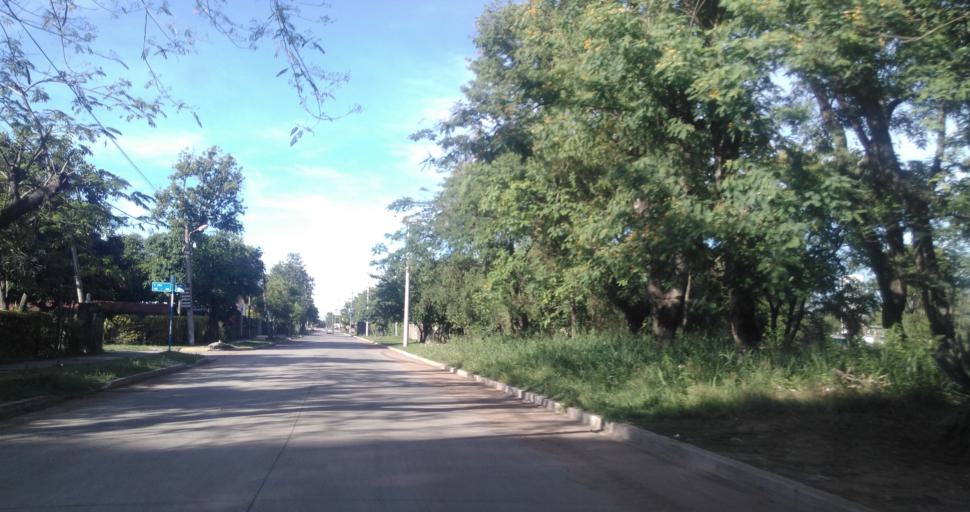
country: AR
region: Chaco
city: Fontana
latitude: -27.4187
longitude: -59.0328
